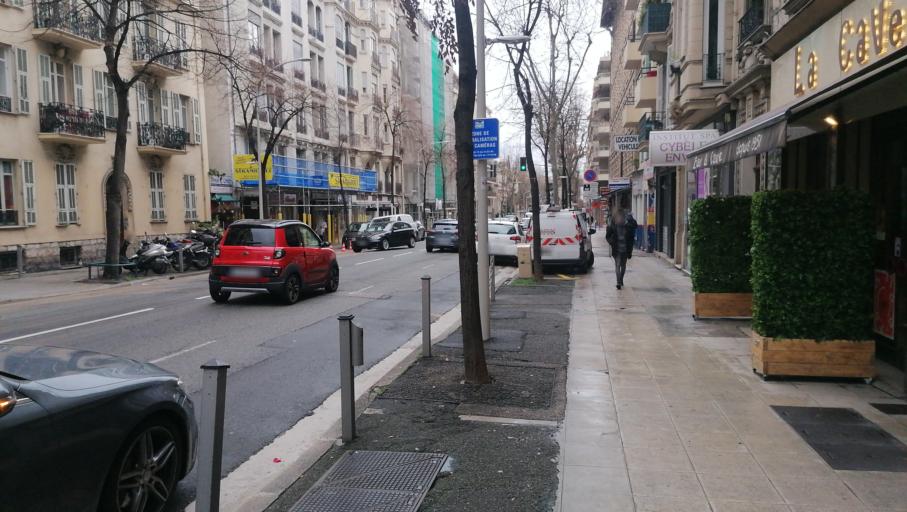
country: FR
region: Provence-Alpes-Cote d'Azur
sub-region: Departement des Alpes-Maritimes
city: Nice
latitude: 43.7055
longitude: 7.2561
